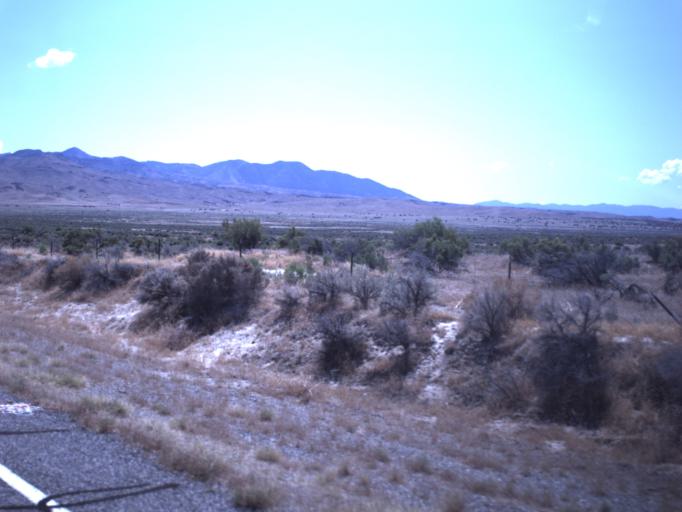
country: US
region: Utah
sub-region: Millard County
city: Delta
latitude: 39.3541
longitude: -112.4282
